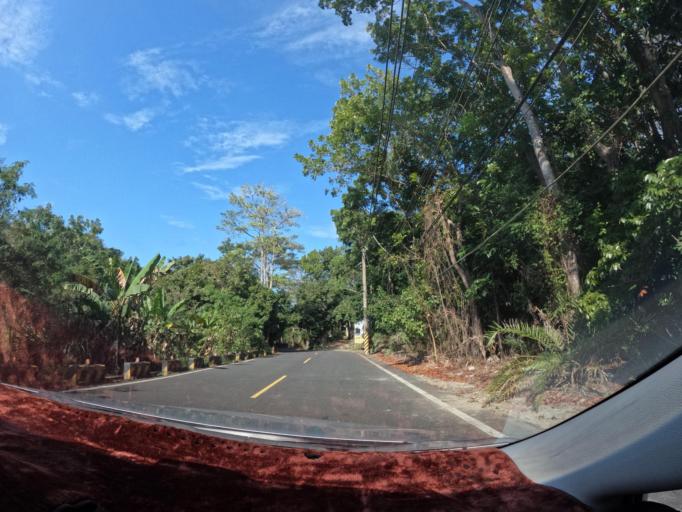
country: TW
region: Taiwan
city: Yujing
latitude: 23.0143
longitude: 120.3982
